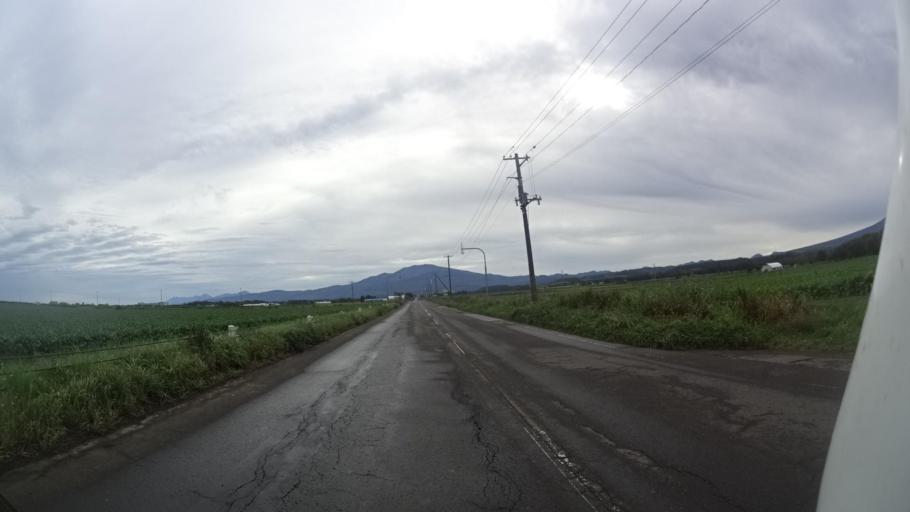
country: JP
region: Hokkaido
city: Abashiri
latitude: 43.8717
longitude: 144.6881
